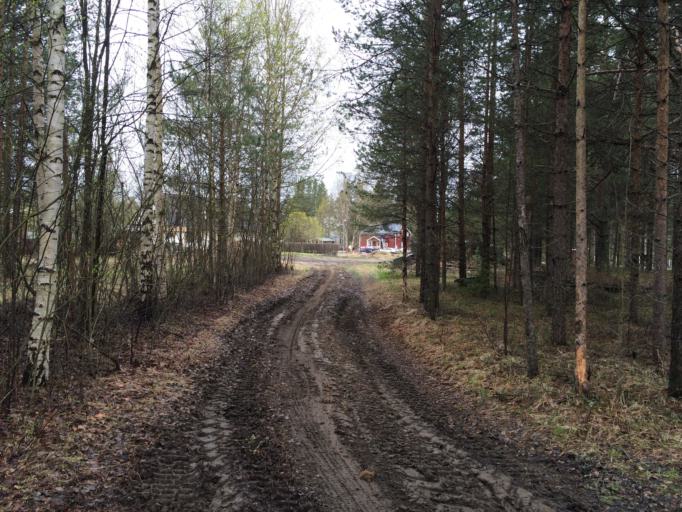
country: SE
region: Norrbotten
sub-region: Bodens Kommun
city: Saevast
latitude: 65.7063
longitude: 21.8160
